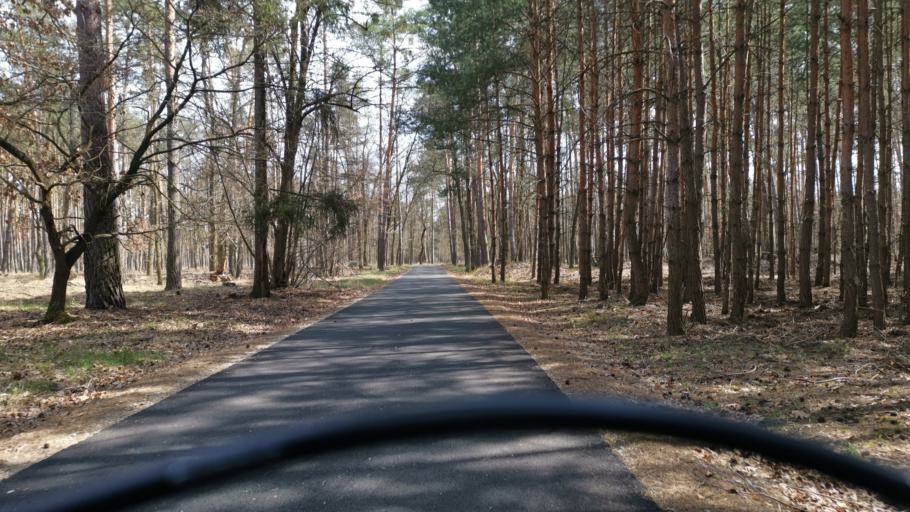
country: SK
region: Trnavsky
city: Gbely
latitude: 48.7150
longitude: 17.0549
